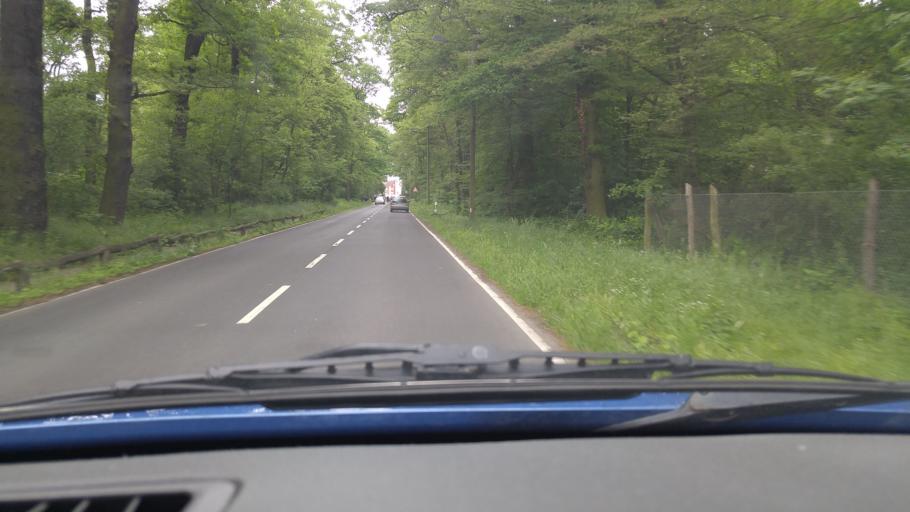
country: DE
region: Hesse
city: Niederrad
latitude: 50.0788
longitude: 8.5780
